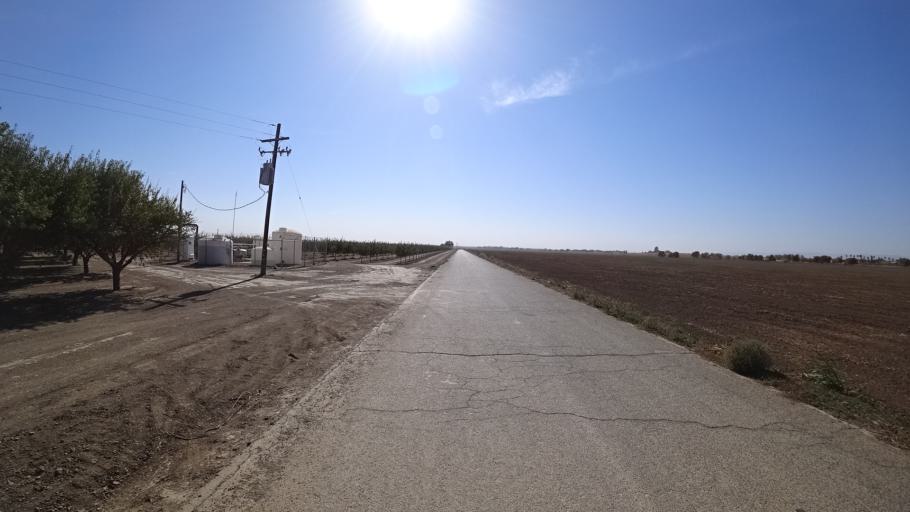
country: US
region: California
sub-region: Yolo County
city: Woodland
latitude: 38.6389
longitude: -121.7570
